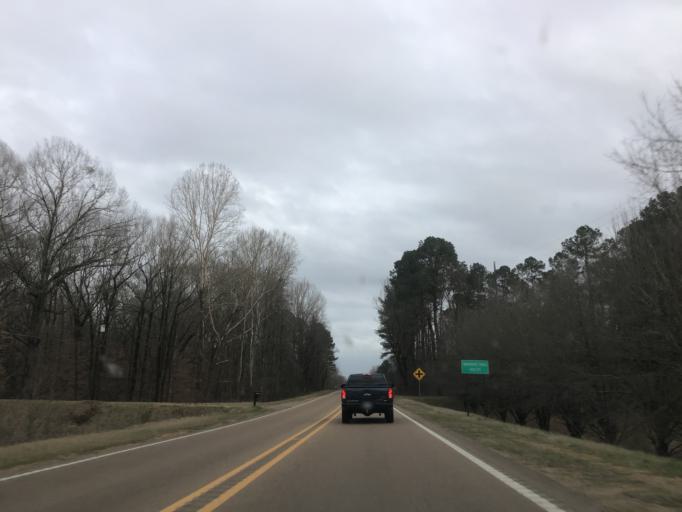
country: US
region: Mississippi
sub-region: Warren County
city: Beechwood
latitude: 32.3207
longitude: -90.8145
